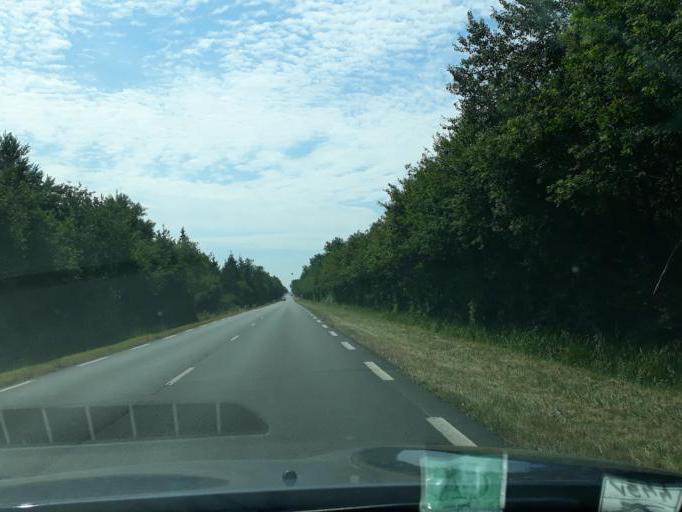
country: FR
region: Centre
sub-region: Departement du Loiret
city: Menestreau-en-Villette
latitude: 47.6608
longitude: 1.9806
